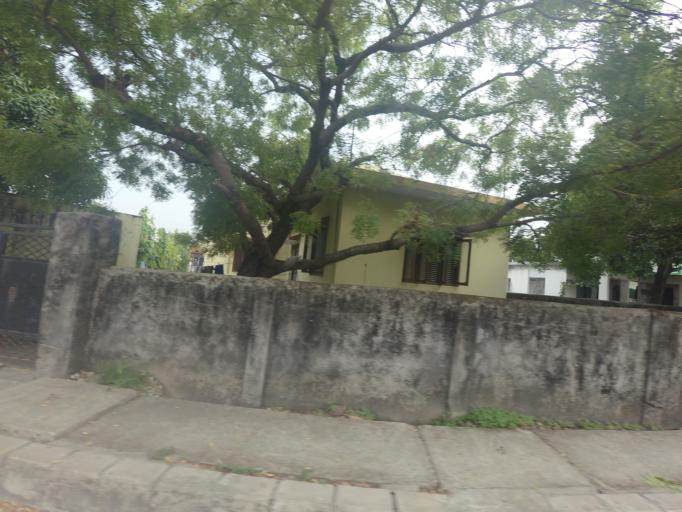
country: NP
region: Western Region
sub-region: Lumbini Zone
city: Bhairahawa
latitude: 27.4898
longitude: 83.4445
